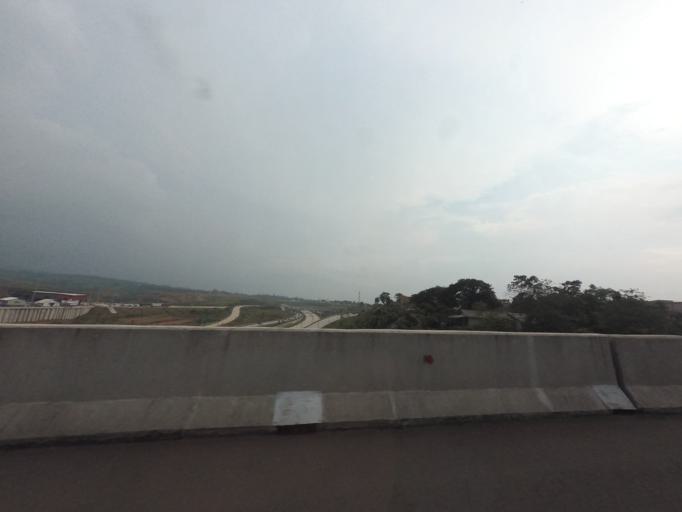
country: ID
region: West Java
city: Cicurug
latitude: -6.7520
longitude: 106.8019
